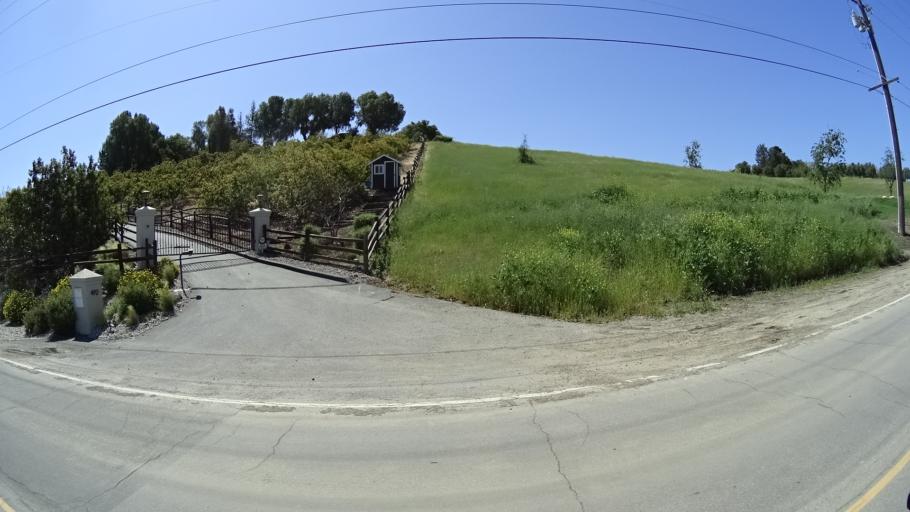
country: US
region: California
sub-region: Ventura County
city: Moorpark
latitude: 34.2499
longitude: -118.8623
